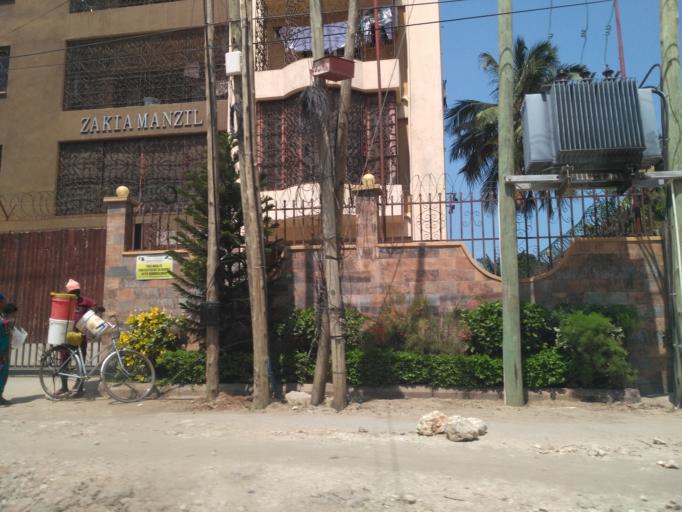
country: TZ
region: Dar es Salaam
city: Dar es Salaam
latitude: -6.8068
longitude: 39.2832
